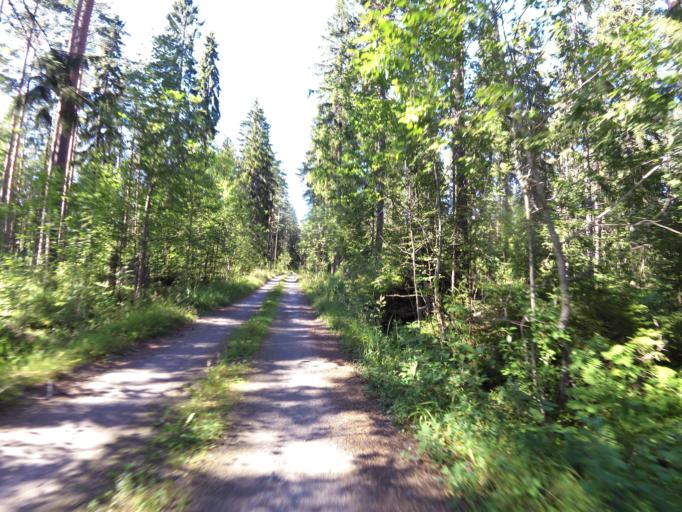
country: SE
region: Gaevleborg
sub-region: Hofors Kommun
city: Hofors
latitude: 60.5728
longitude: 16.4252
